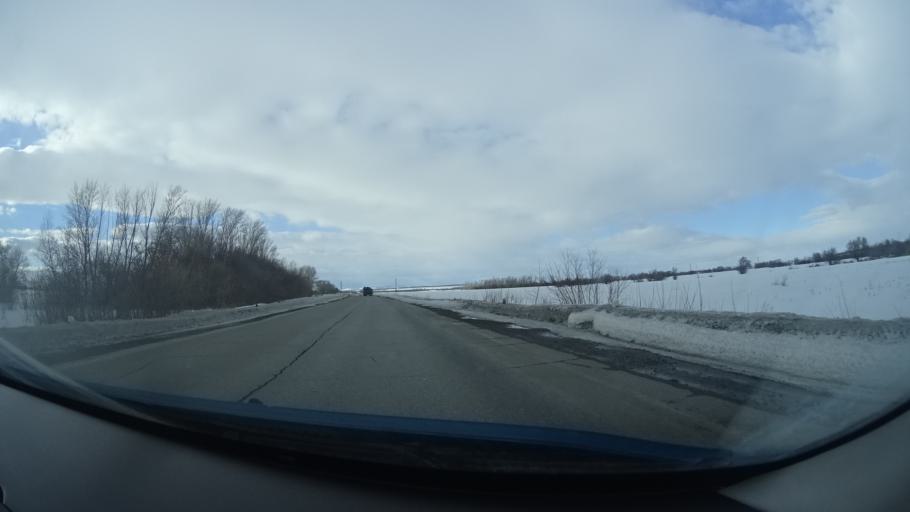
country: RU
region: Chelyabinsk
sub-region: Gorod Magnitogorsk
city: Magnitogorsk
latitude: 53.5799
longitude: 58.8879
